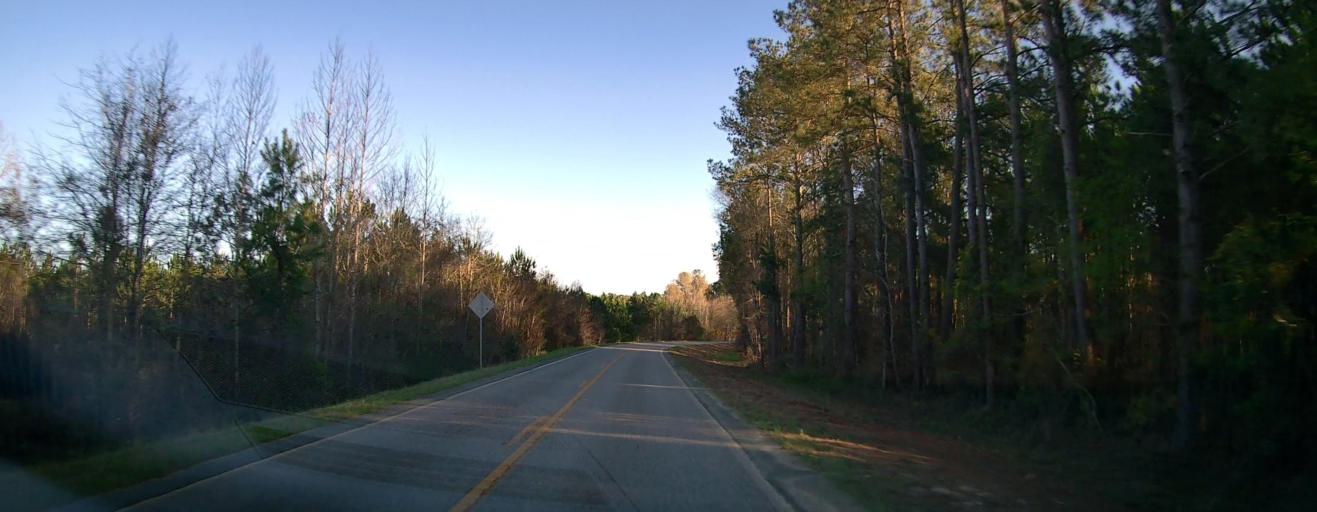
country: US
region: Georgia
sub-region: Wilcox County
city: Abbeville
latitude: 32.0813
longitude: -83.2884
